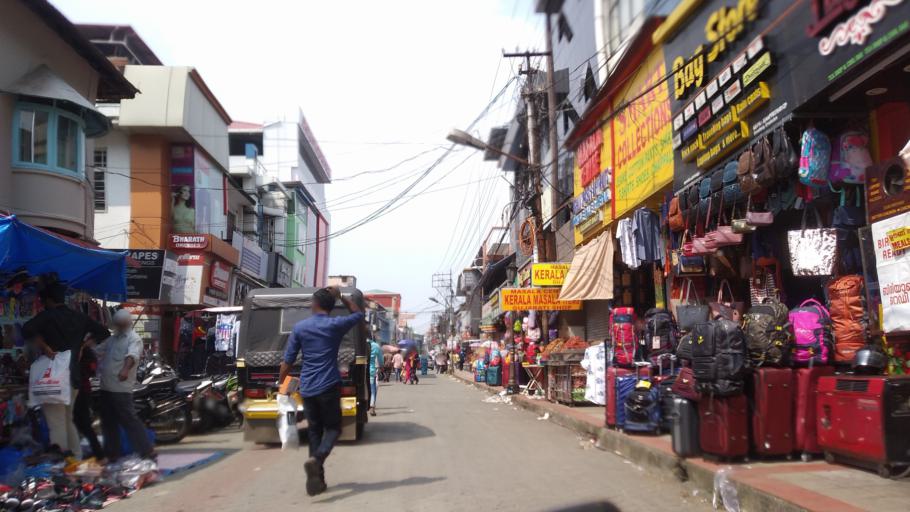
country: IN
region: Kerala
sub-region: Ernakulam
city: Cochin
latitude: 9.9777
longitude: 76.2778
